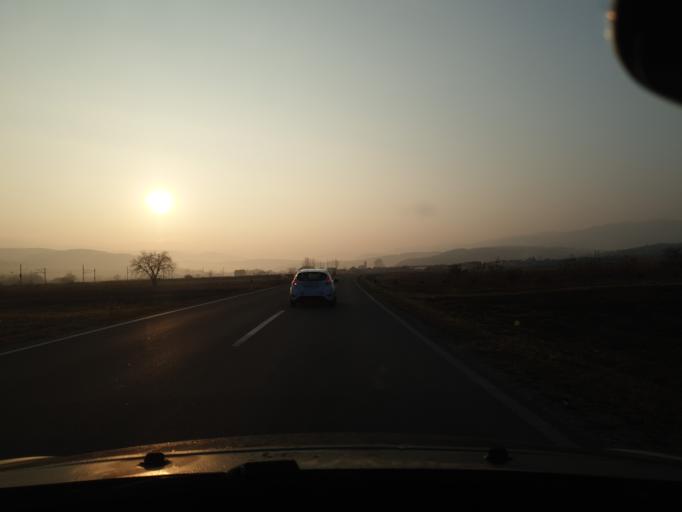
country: RS
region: Central Serbia
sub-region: Jablanicki Okrug
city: Leskovac
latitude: 42.9337
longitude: 22.0116
